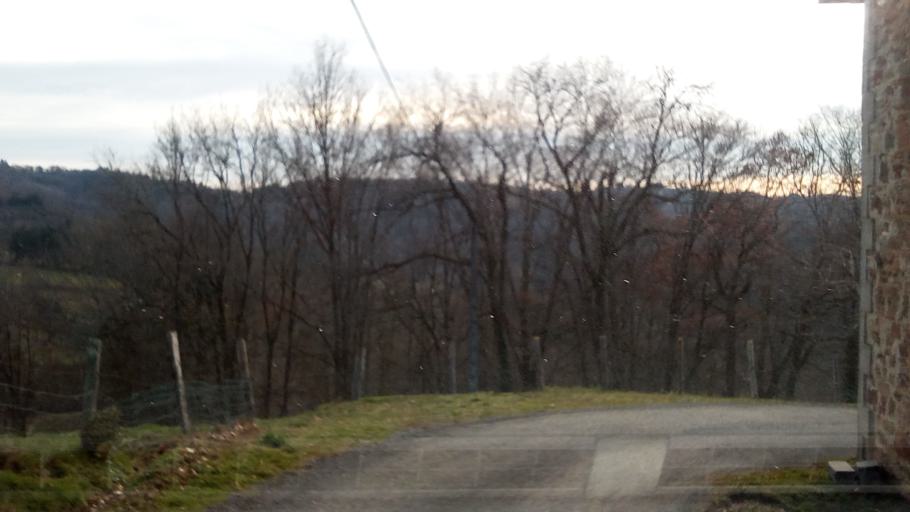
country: FR
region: Limousin
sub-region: Departement de la Correze
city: Naves
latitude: 45.3106
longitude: 1.7921
